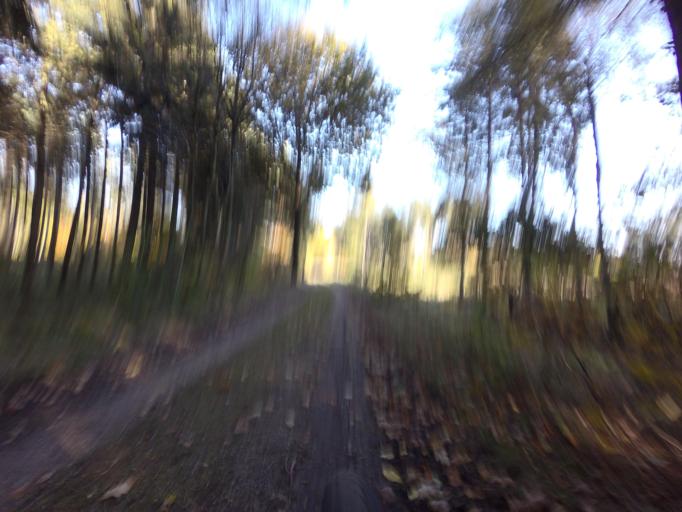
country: DK
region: Central Jutland
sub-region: Norddjurs Kommune
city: Grenaa
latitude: 56.4911
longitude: 10.6870
